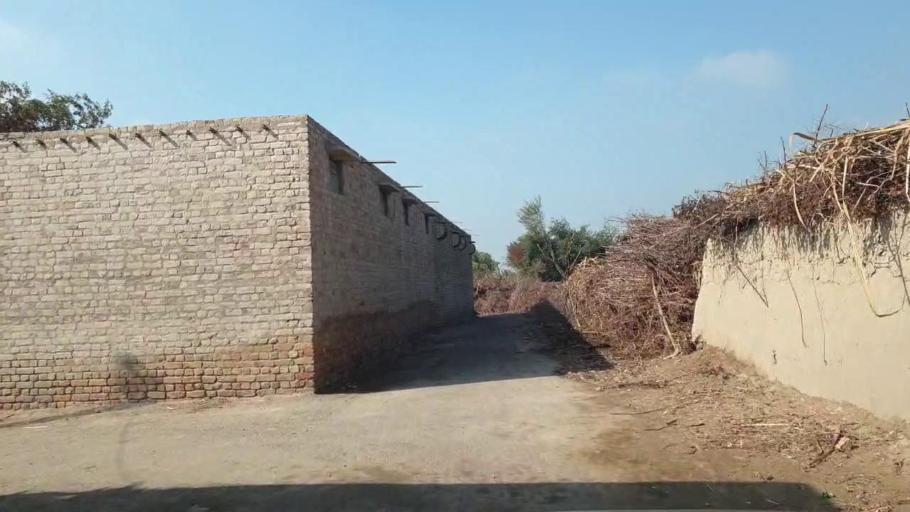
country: PK
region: Sindh
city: Shahdadpur
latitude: 26.0164
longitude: 68.5931
